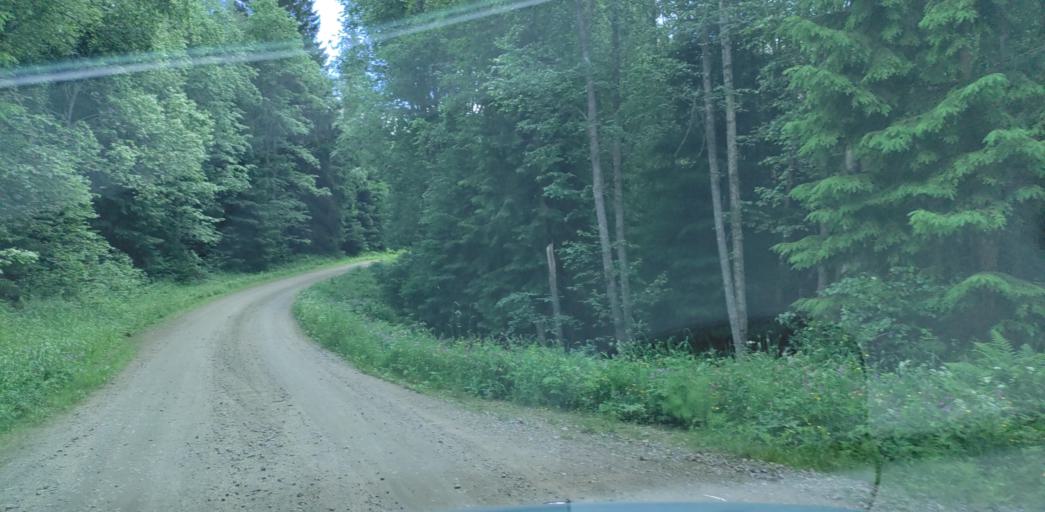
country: SE
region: Vaermland
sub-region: Hagfors Kommun
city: Ekshaerad
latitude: 60.1044
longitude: 13.3196
